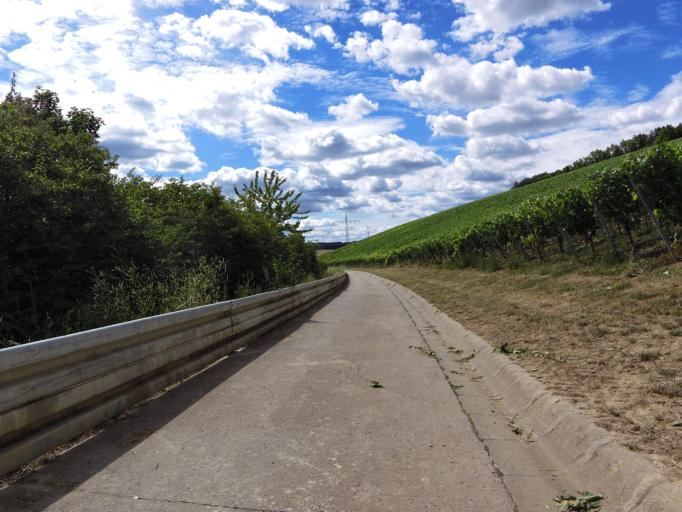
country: DE
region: Bavaria
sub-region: Regierungsbezirk Unterfranken
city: Veitshochheim
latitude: 49.8171
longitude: 9.8885
